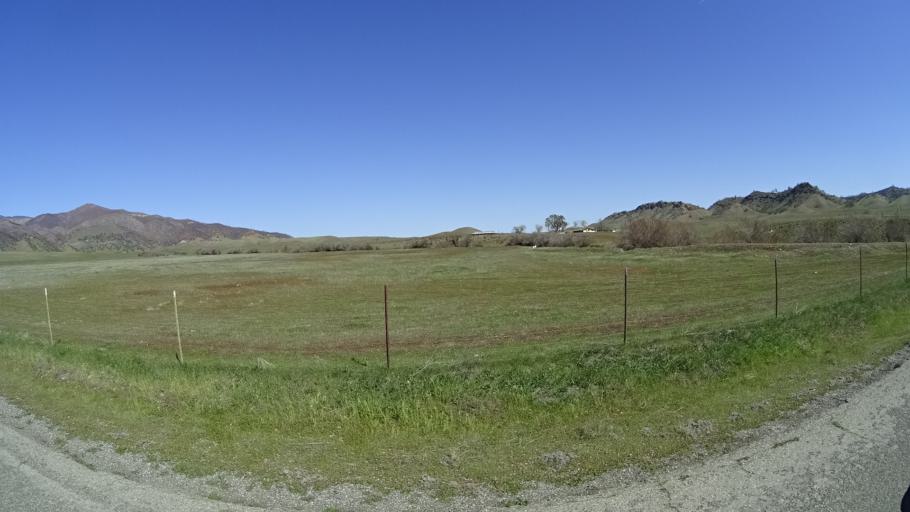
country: US
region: California
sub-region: Tehama County
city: Rancho Tehama Reserve
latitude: 39.6994
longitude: -122.5530
